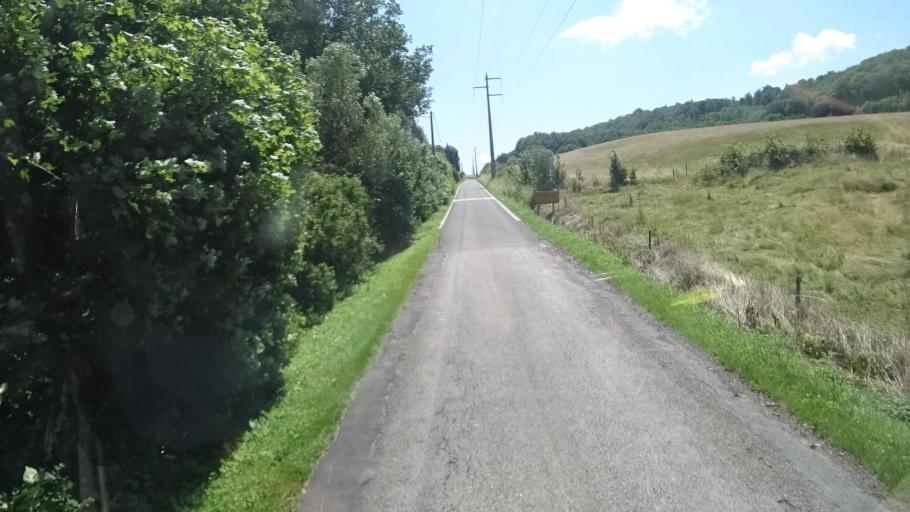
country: BE
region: Wallonia
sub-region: Province de Namur
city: Profondeville
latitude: 50.3602
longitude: 4.8239
